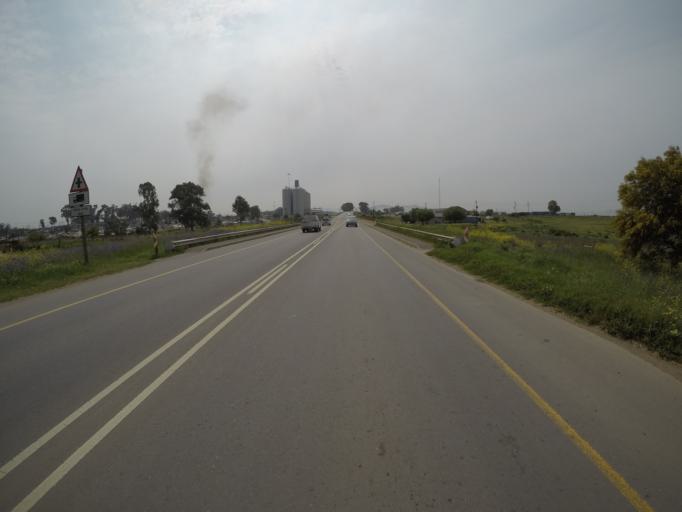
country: ZA
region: Western Cape
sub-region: City of Cape Town
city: Kraaifontein
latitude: -33.7063
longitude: 18.6998
